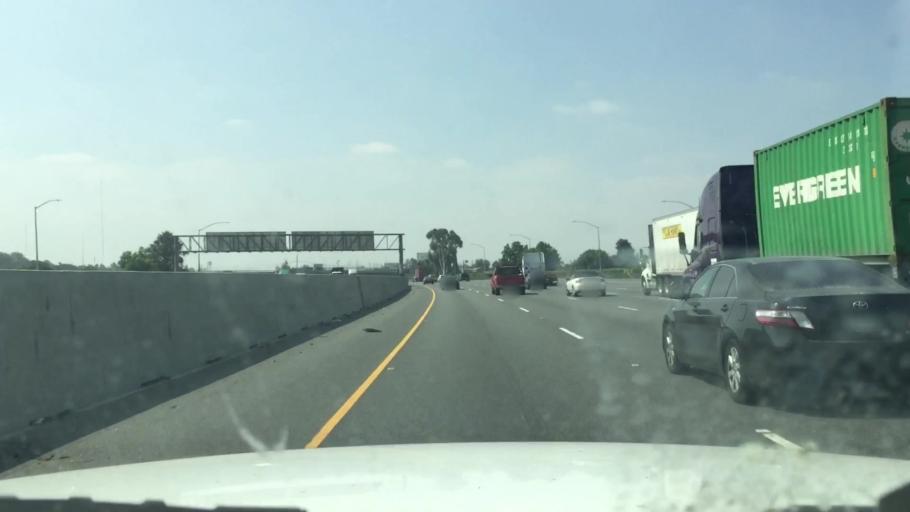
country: US
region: California
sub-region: Los Angeles County
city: East Rancho Dominguez
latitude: 33.9053
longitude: -118.1891
